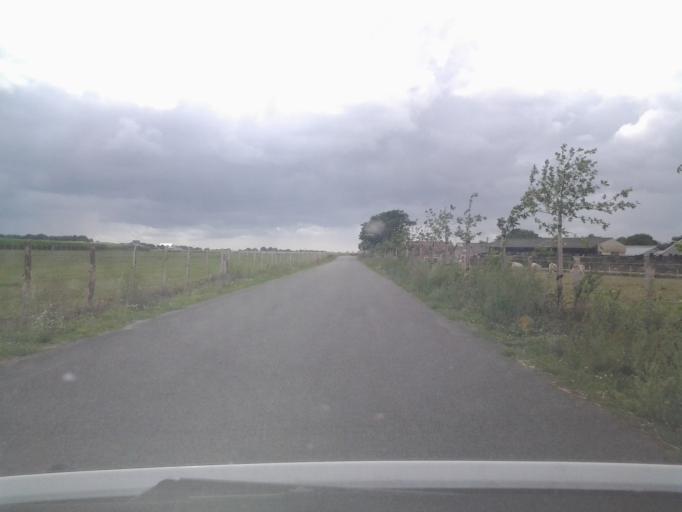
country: FR
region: Pays de la Loire
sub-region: Departement de la Vendee
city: Dompierre-sur-Yon
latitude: 46.7017
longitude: -1.3643
